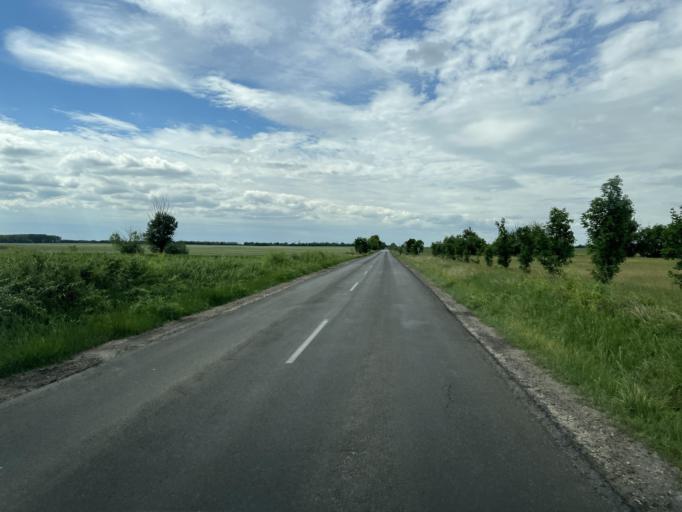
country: HU
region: Pest
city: Szentlorinckata
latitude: 47.5060
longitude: 19.7416
